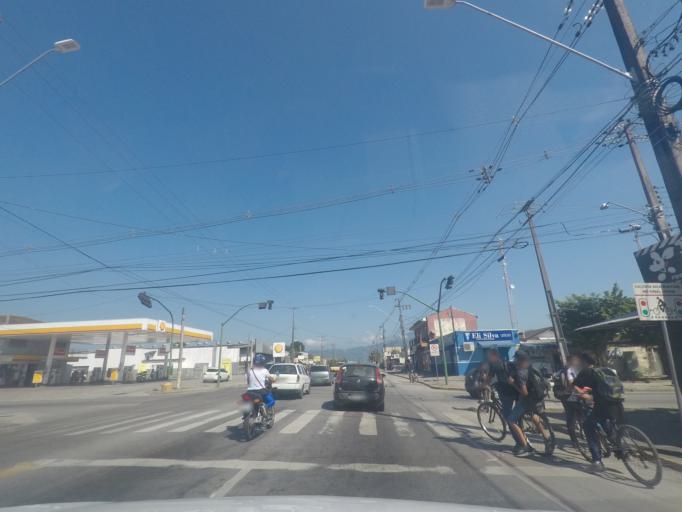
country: BR
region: Parana
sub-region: Paranagua
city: Paranagua
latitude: -25.5593
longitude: -48.5599
